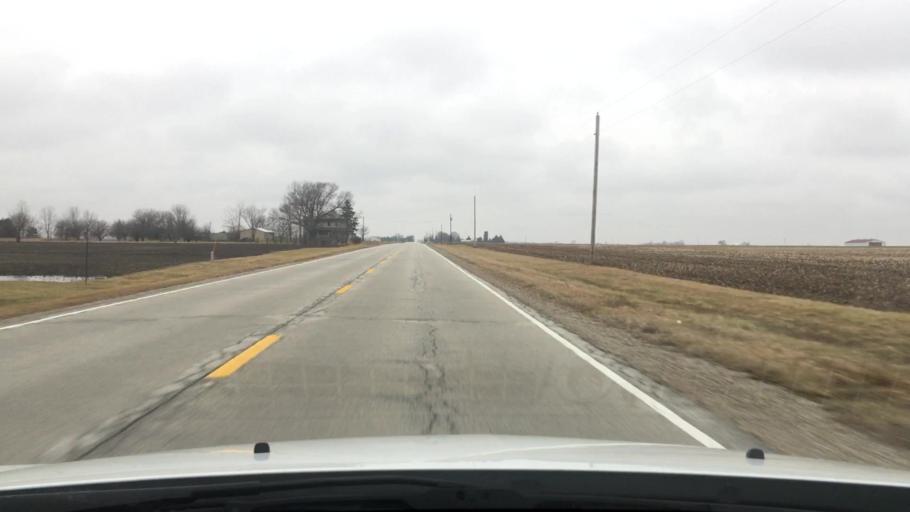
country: US
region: Illinois
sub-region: Iroquois County
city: Clifton
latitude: 40.8858
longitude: -87.9128
